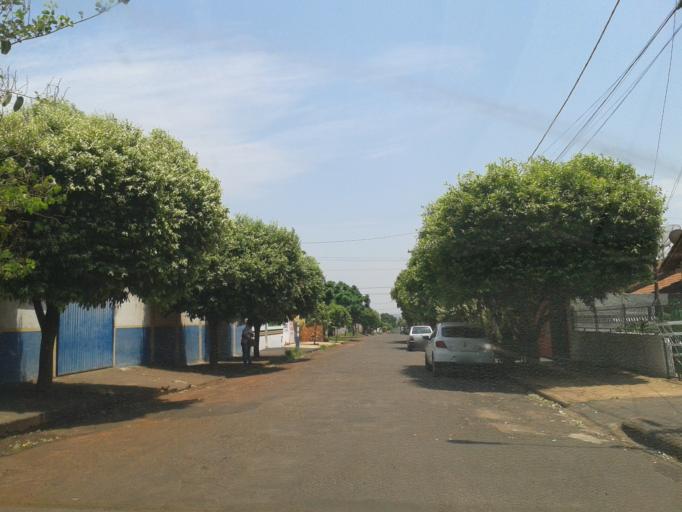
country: BR
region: Minas Gerais
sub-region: Ituiutaba
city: Ituiutaba
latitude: -18.9848
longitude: -49.4464
